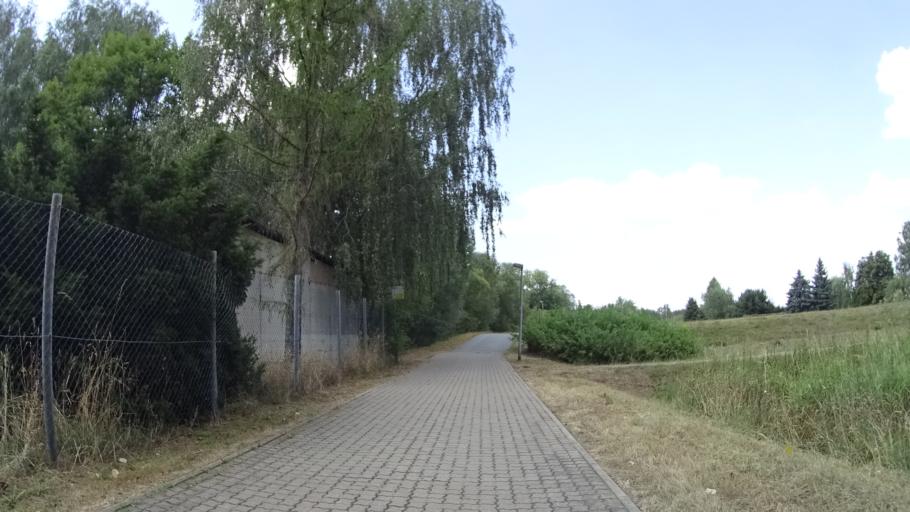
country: DE
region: Saxony
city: Ostritz
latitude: 51.0202
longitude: 14.9321
